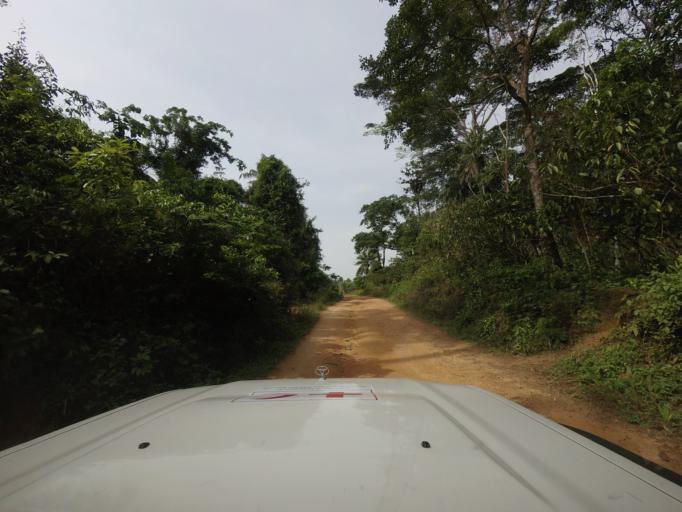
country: GN
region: Nzerekore
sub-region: Macenta
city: Macenta
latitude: 8.4782
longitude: -9.5526
